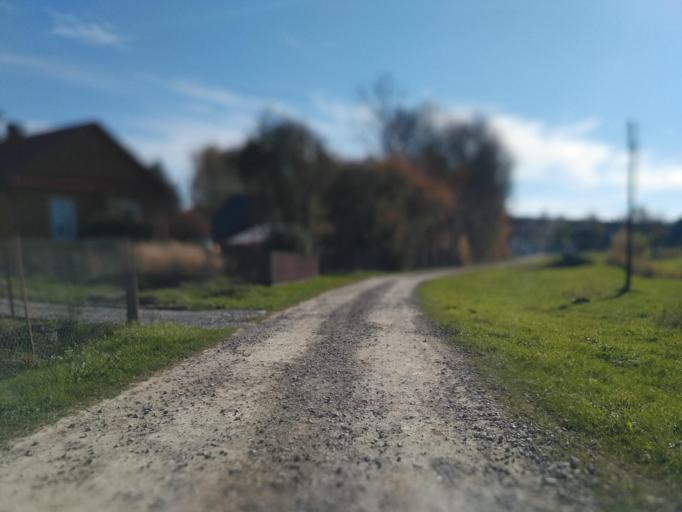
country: PL
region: Subcarpathian Voivodeship
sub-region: Powiat ropczycko-sedziszowski
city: Iwierzyce
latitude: 50.0189
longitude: 21.7586
